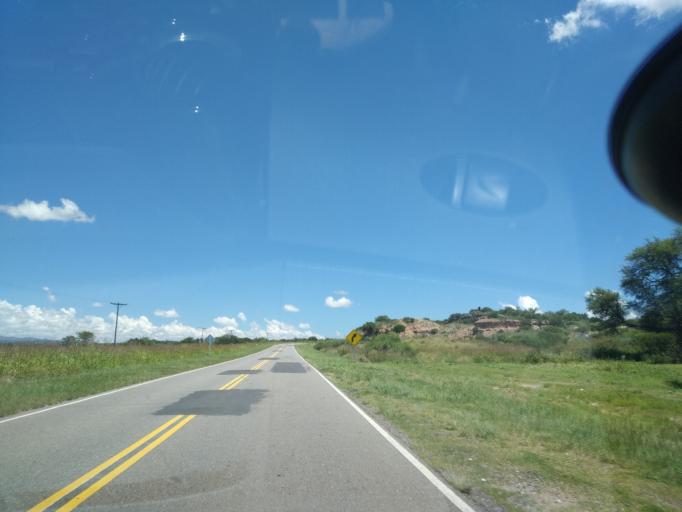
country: AR
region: Cordoba
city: Salsacate
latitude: -31.4047
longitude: -65.0964
